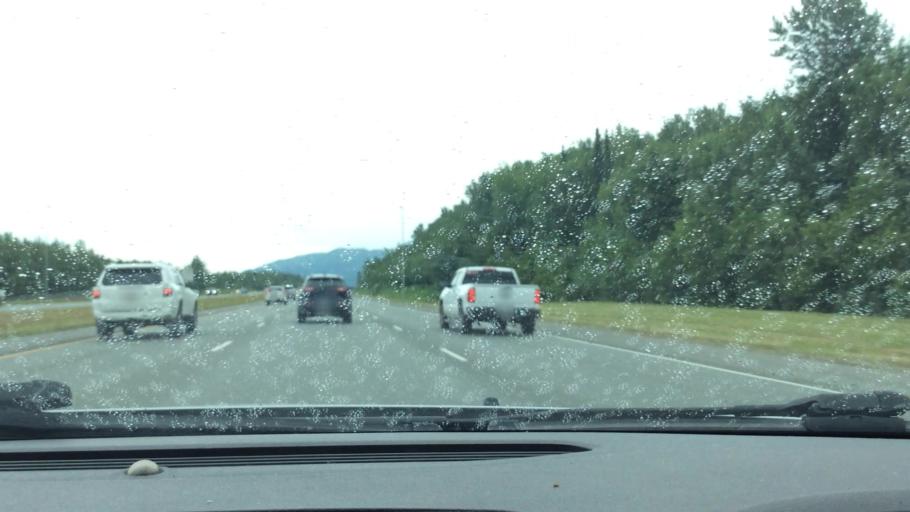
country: US
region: Alaska
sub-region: Anchorage Municipality
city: Elmendorf Air Force Base
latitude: 61.2417
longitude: -149.6866
